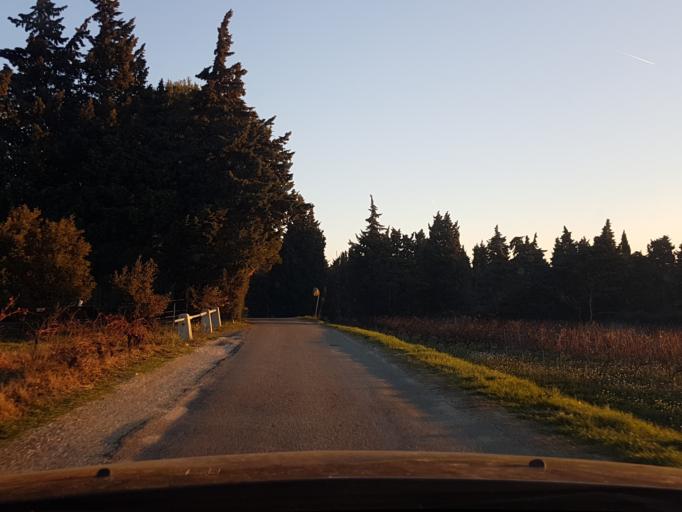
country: FR
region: Provence-Alpes-Cote d'Azur
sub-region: Departement du Vaucluse
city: Saint-Saturnin-les-Avignon
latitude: 43.9582
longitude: 4.9150
